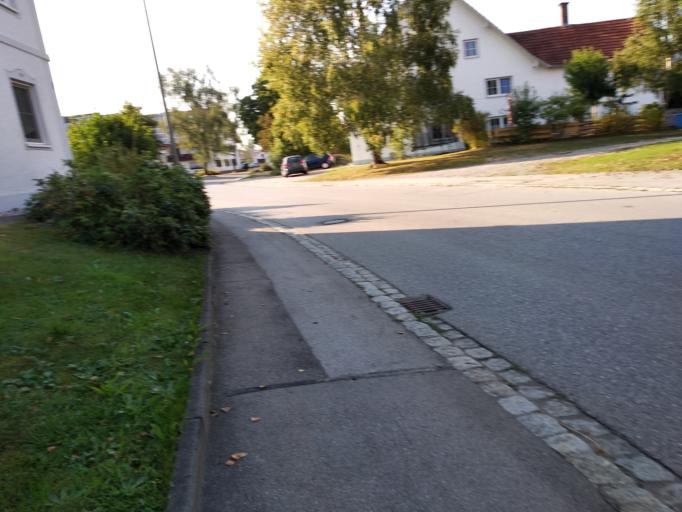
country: DE
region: Bavaria
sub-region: Swabia
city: Westerheim
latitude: 48.0192
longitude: 10.3006
